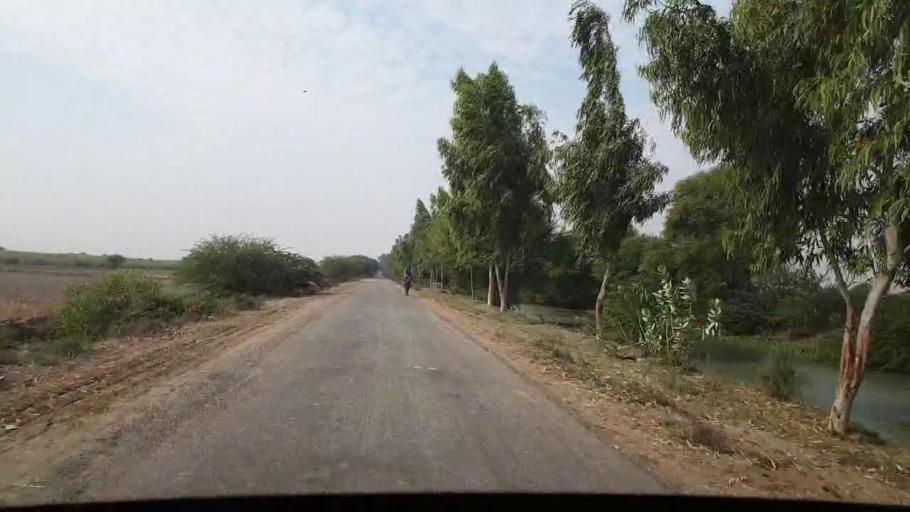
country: PK
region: Sindh
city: Chuhar Jamali
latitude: 24.3909
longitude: 67.9541
